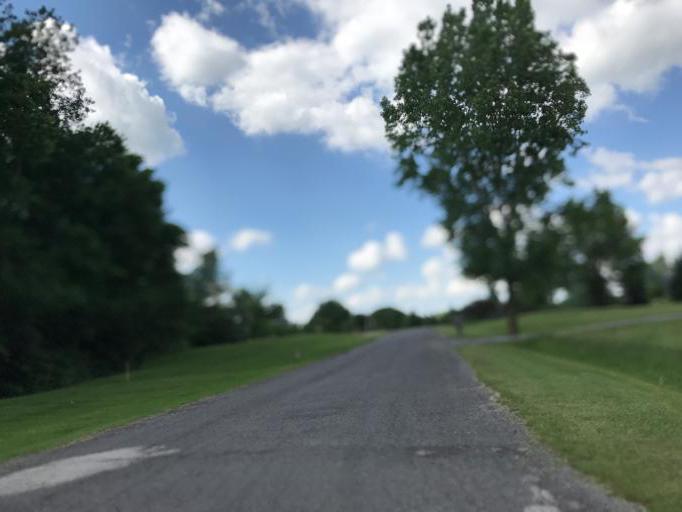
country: US
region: Michigan
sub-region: Oakland County
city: South Lyon
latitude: 42.4260
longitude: -83.6587
